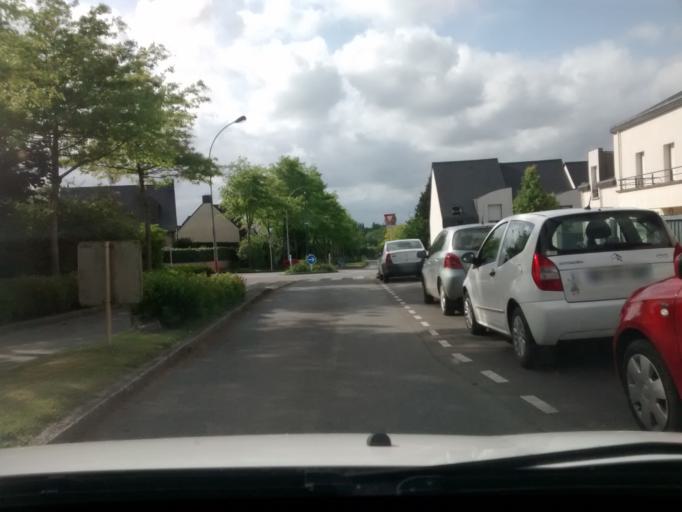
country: FR
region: Brittany
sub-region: Departement d'Ille-et-Vilaine
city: Chateaugiron
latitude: 48.0634
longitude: -1.5258
